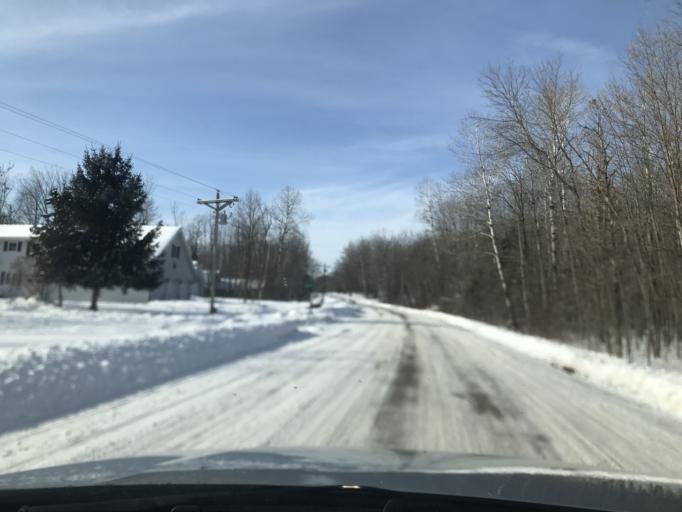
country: US
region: Wisconsin
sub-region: Oconto County
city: Oconto Falls
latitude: 45.1567
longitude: -88.1954
